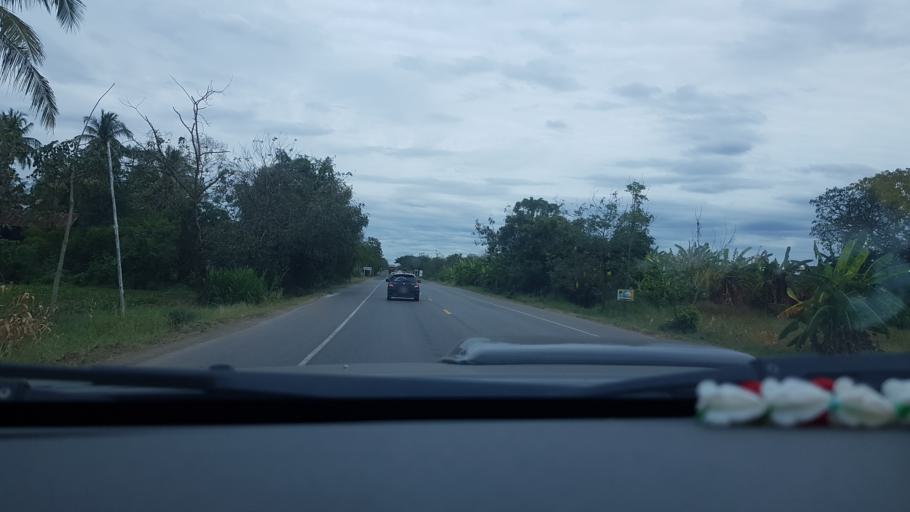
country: TH
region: Phetchabun
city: Phetchabun
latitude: 16.4626
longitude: 101.1220
